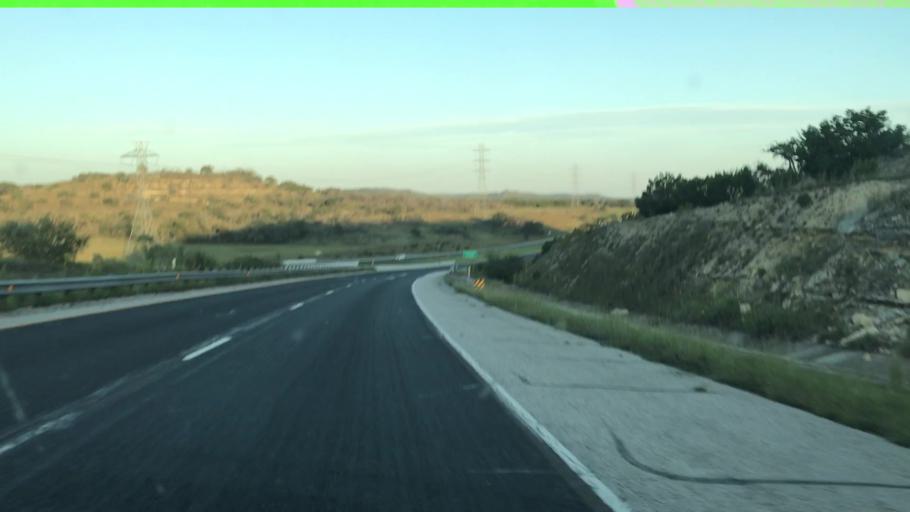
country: US
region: Texas
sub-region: Kerr County
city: Kerrville
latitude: 30.0529
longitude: -99.0137
